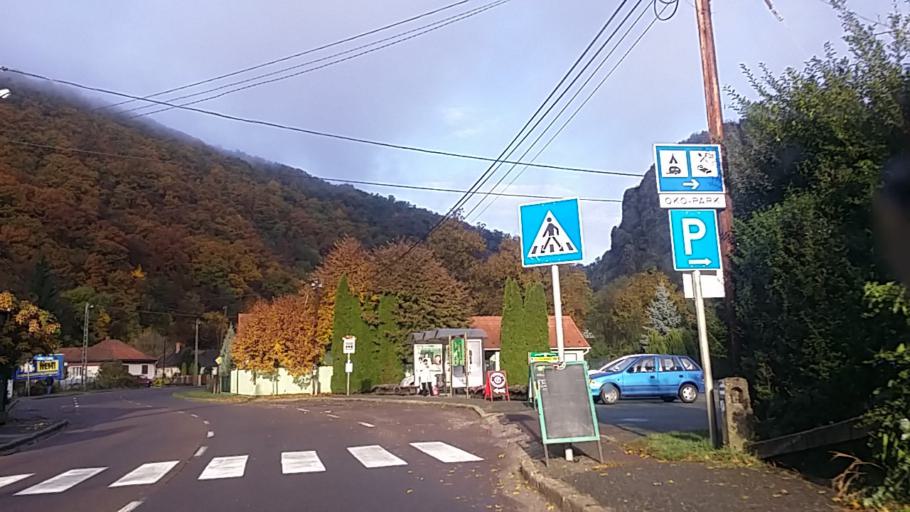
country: HU
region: Heves
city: Belapatfalva
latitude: 47.9880
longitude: 20.3312
